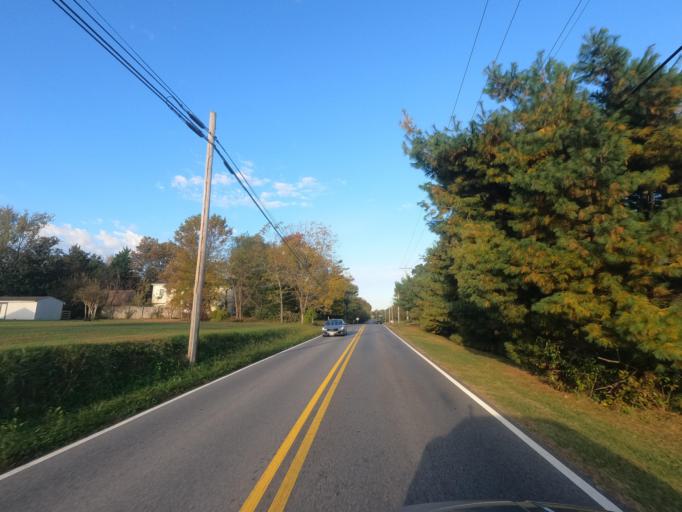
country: US
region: Maryland
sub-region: Calvert County
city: Chesapeake Ranch Estates
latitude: 38.3845
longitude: -76.4207
